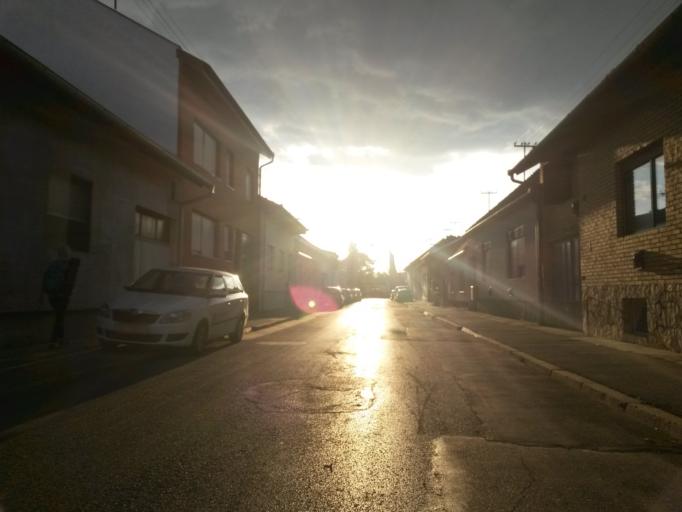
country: HR
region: Osjecko-Baranjska
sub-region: Grad Osijek
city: Osijek
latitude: 45.5462
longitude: 18.7229
